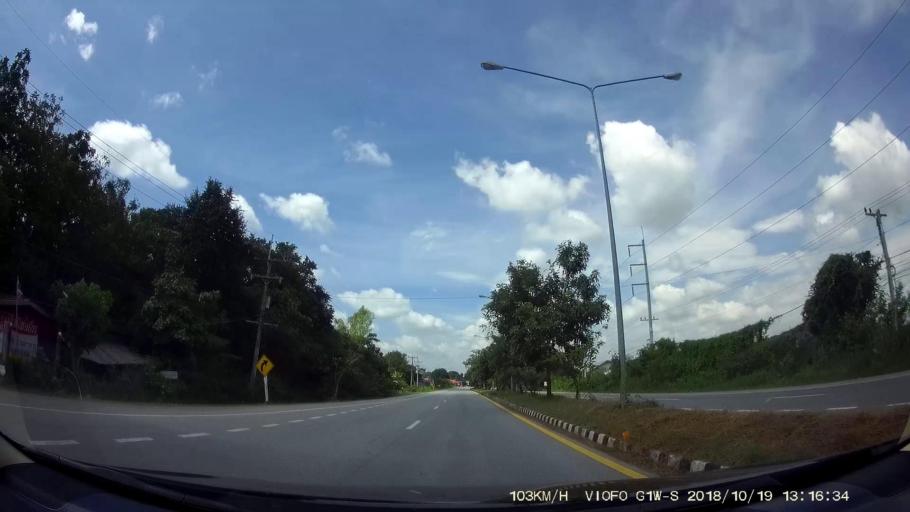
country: TH
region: Chaiyaphum
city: Chatturat
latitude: 15.4057
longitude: 101.8353
